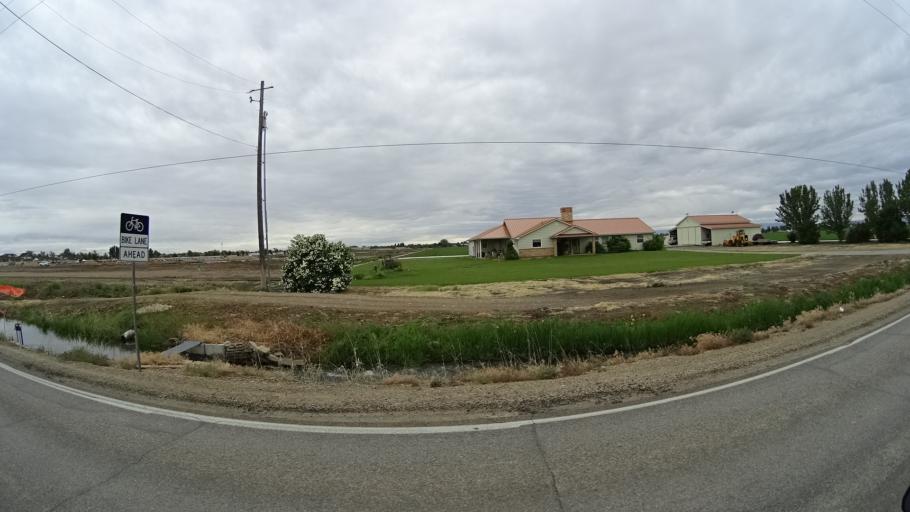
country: US
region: Idaho
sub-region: Ada County
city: Meridian
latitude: 43.6487
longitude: -116.4437
